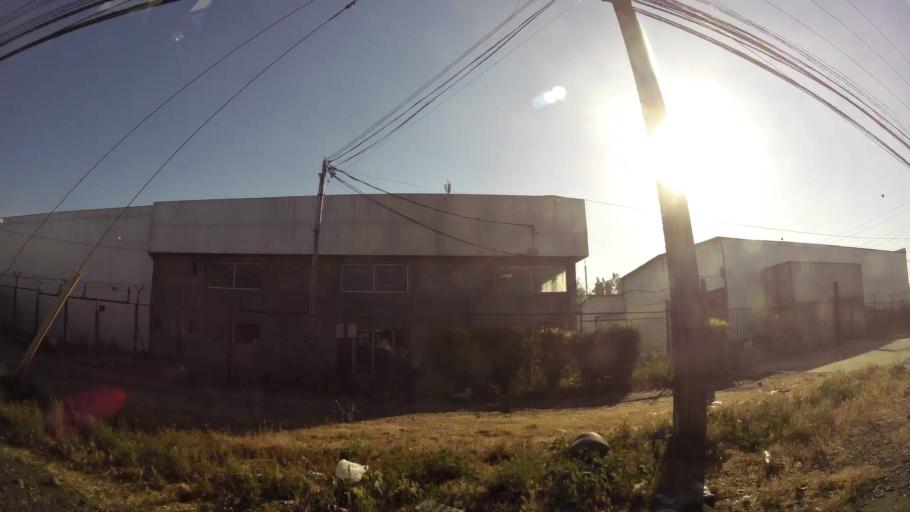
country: CL
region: Santiago Metropolitan
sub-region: Provincia de Maipo
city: San Bernardo
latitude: -33.5331
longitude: -70.7529
